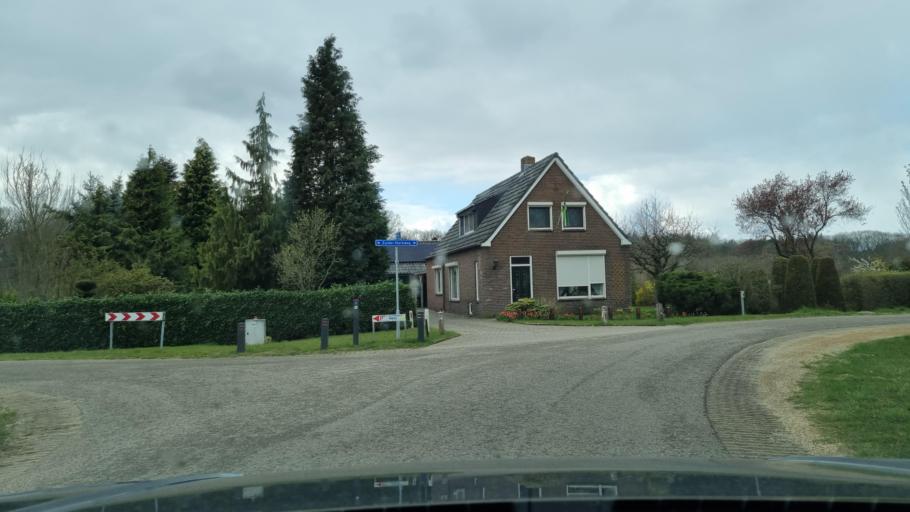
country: NL
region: Gelderland
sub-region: Gemeente Montferland
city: s-Heerenberg
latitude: 51.9002
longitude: 6.1757
